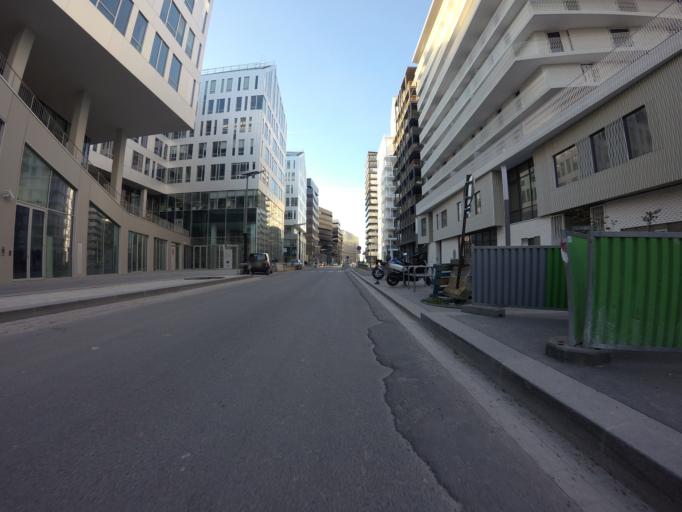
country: FR
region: Ile-de-France
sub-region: Departement des Hauts-de-Seine
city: Clichy
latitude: 48.8898
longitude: 2.3128
